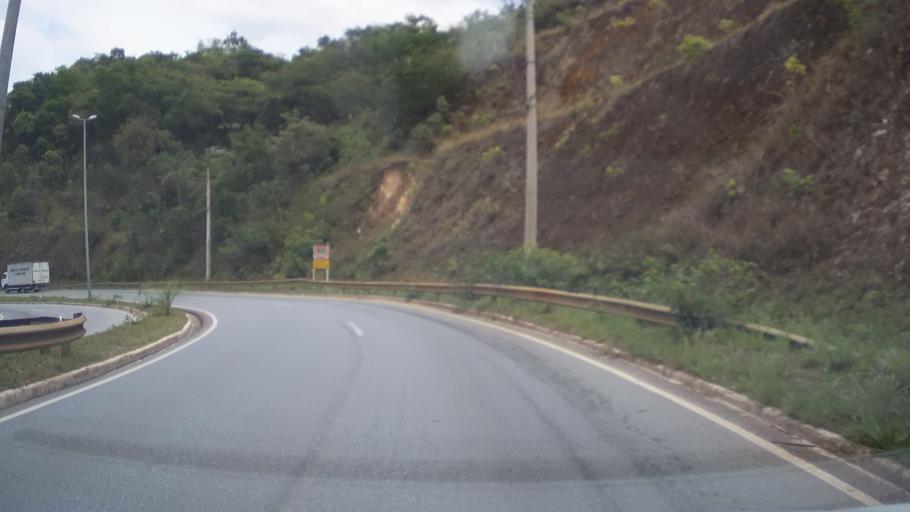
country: BR
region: Minas Gerais
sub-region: Nova Lima
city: Nova Lima
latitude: -19.9961
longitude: -43.9137
